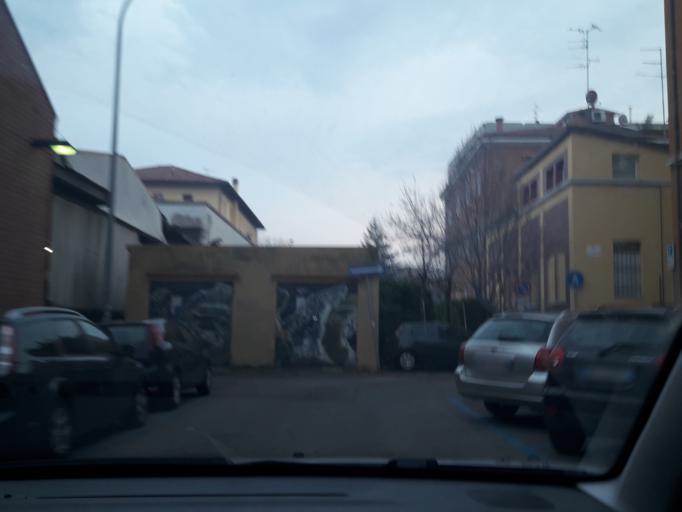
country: IT
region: Emilia-Romagna
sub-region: Provincia di Bologna
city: Bologna
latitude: 44.5024
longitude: 11.3153
